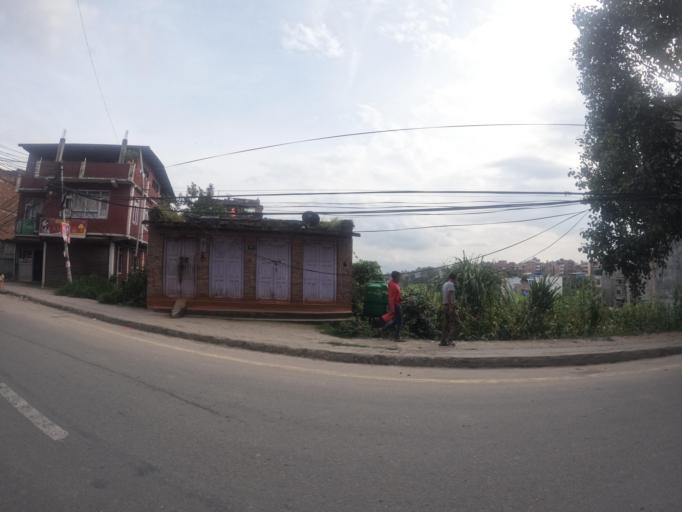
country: NP
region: Central Region
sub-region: Bagmati Zone
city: Bhaktapur
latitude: 27.6825
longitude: 85.3904
